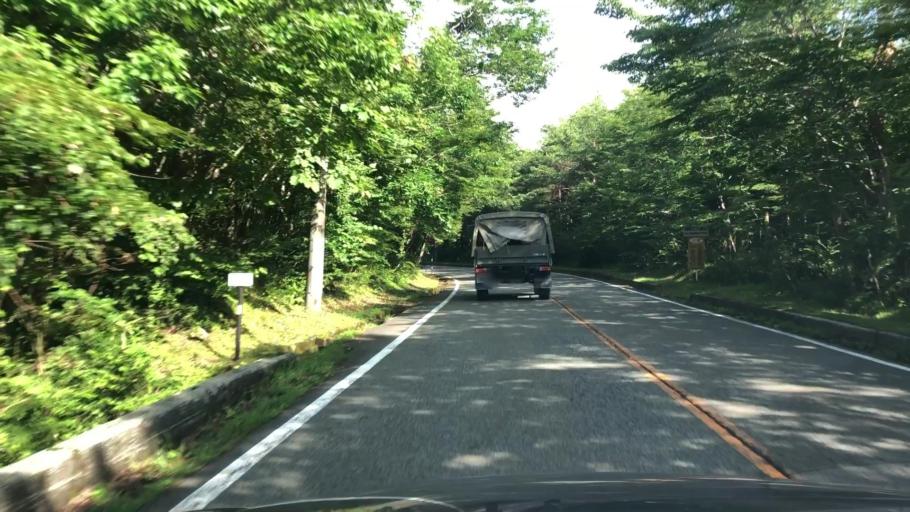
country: JP
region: Shizuoka
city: Gotemba
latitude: 35.3331
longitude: 138.8187
